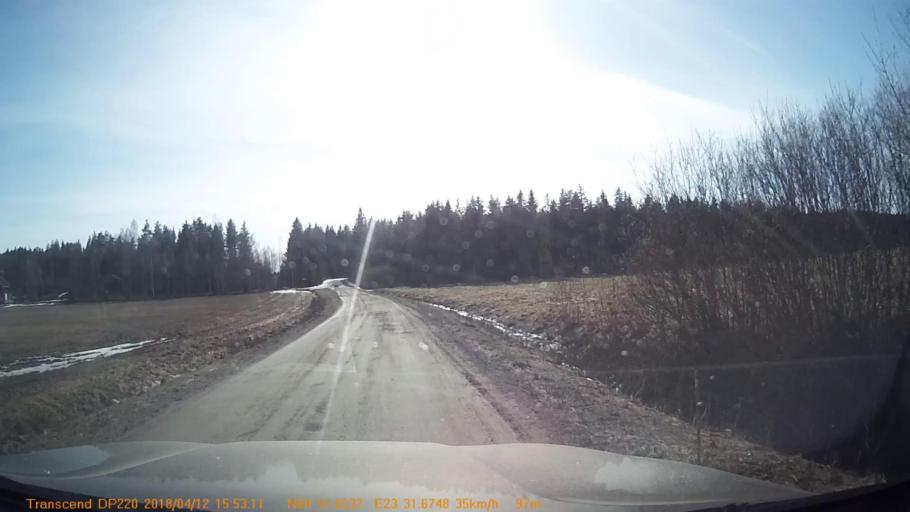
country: FI
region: Haeme
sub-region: Forssa
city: Jokioinen
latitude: 60.8604
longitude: 23.5279
